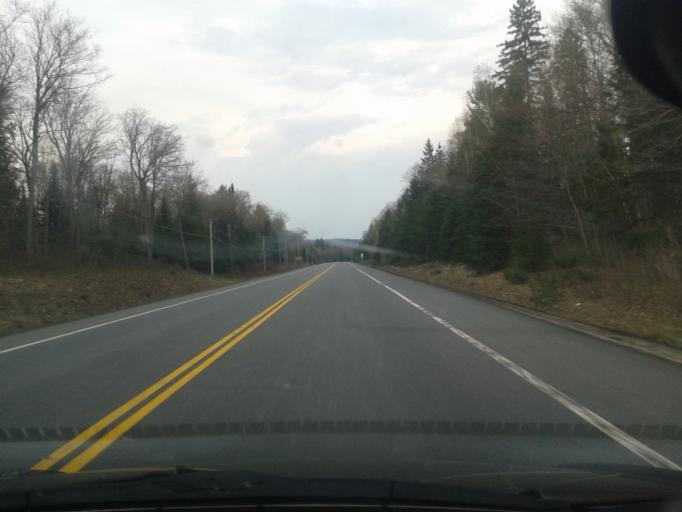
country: CA
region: Ontario
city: Huntsville
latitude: 45.4467
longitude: -78.8170
